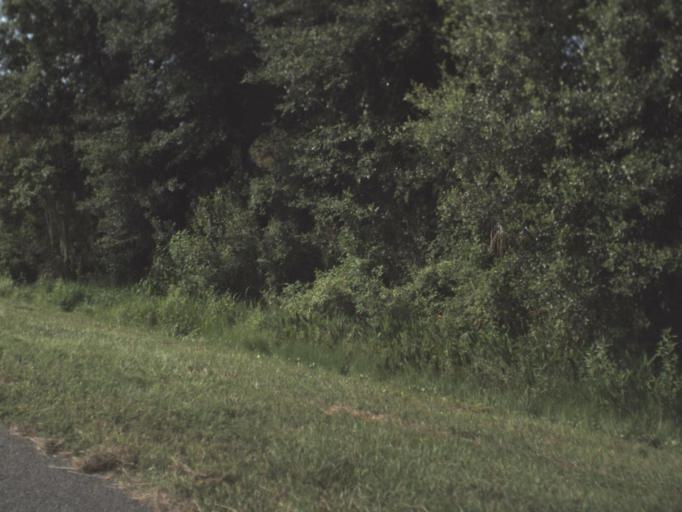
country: US
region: Florida
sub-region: Alachua County
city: Gainesville
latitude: 29.4962
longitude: -82.2586
